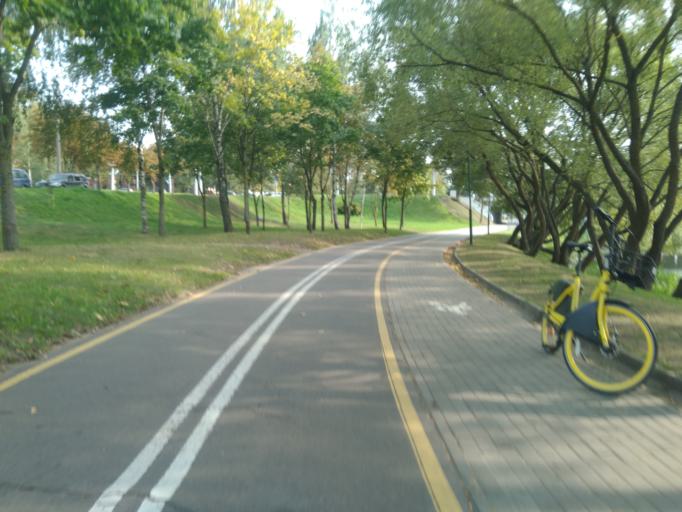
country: BY
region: Minsk
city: Minsk
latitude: 53.8752
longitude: 27.5842
